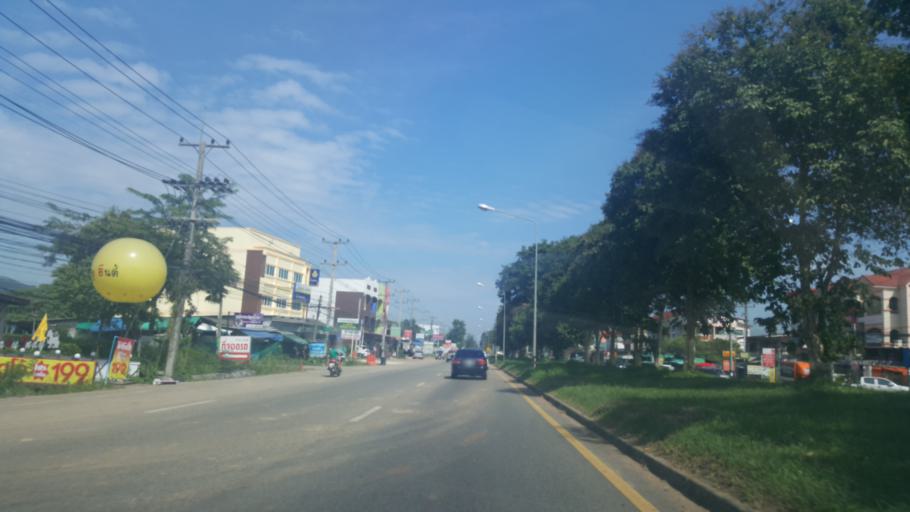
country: TH
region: Chon Buri
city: Sattahip
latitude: 12.7062
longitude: 100.8895
